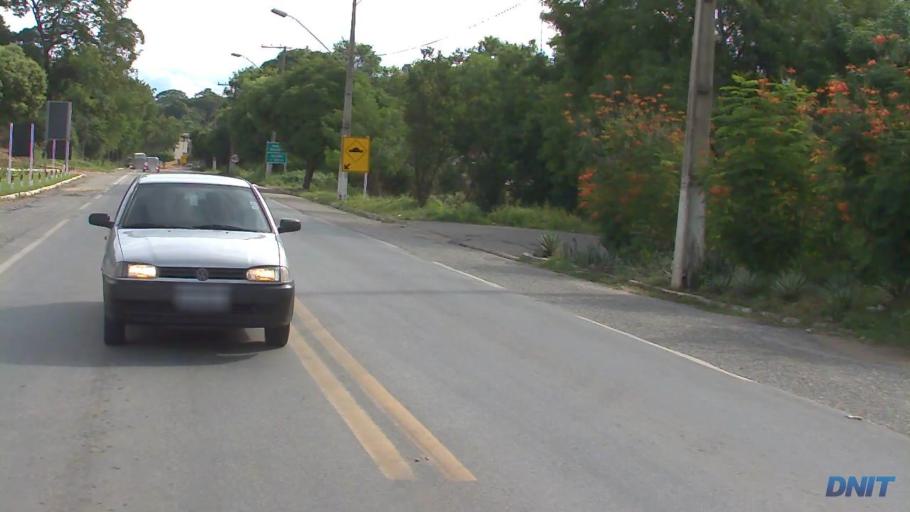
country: BR
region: Minas Gerais
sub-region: Belo Oriente
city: Belo Oriente
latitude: -19.2286
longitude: -42.3261
